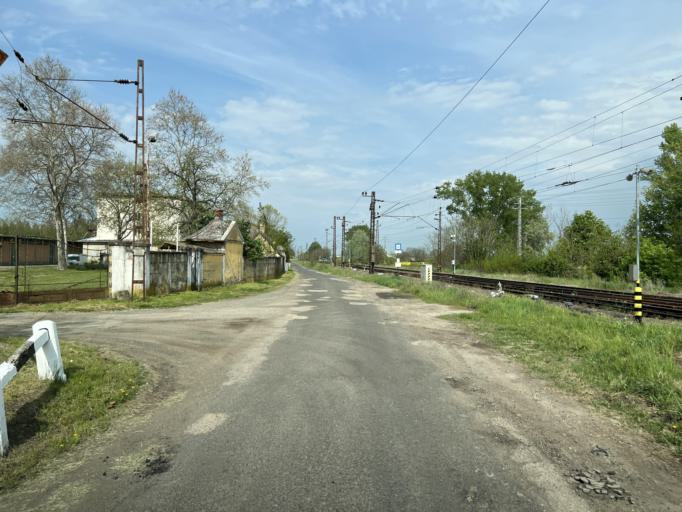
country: HU
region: Pest
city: Tapioszele
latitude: 47.3485
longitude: 19.8642
